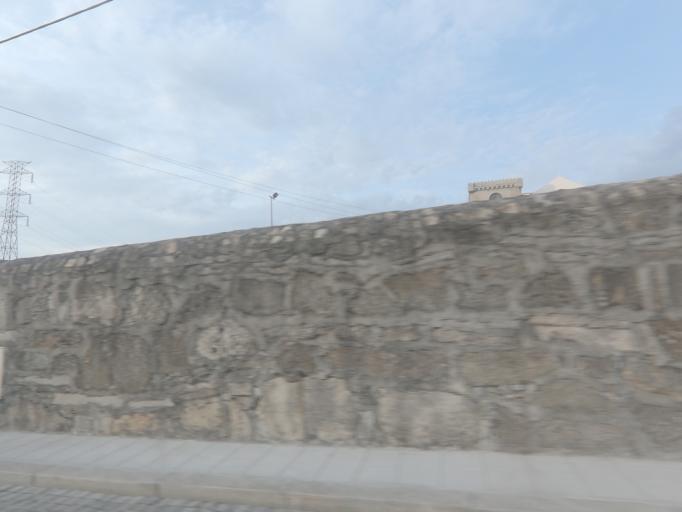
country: PT
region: Porto
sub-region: Maia
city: Leca do Bailio
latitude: 41.2050
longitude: -8.6185
